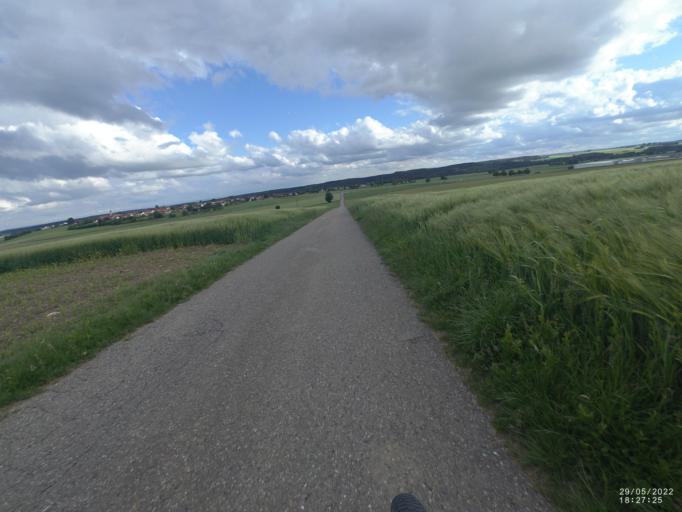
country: DE
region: Baden-Wuerttemberg
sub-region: Tuebingen Region
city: Ballendorf
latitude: 48.6010
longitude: 10.0964
